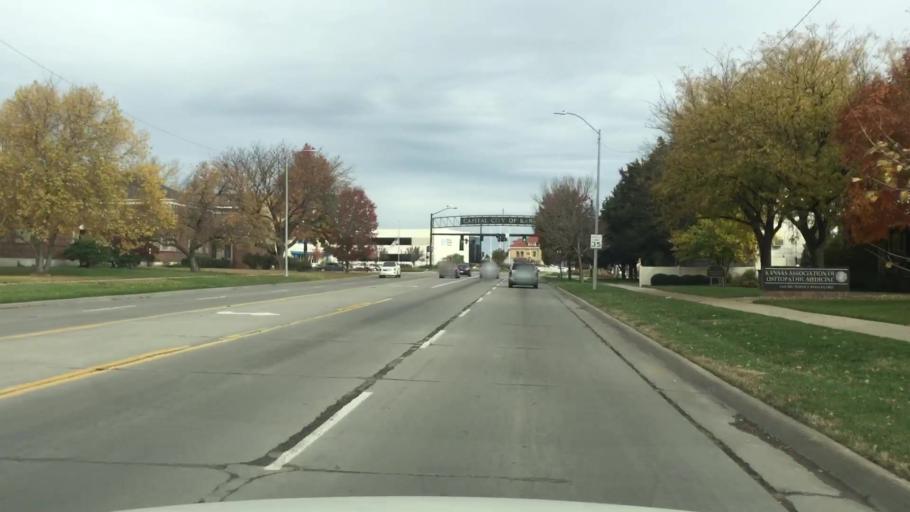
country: US
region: Kansas
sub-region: Shawnee County
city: Topeka
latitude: 39.0430
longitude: -95.6828
